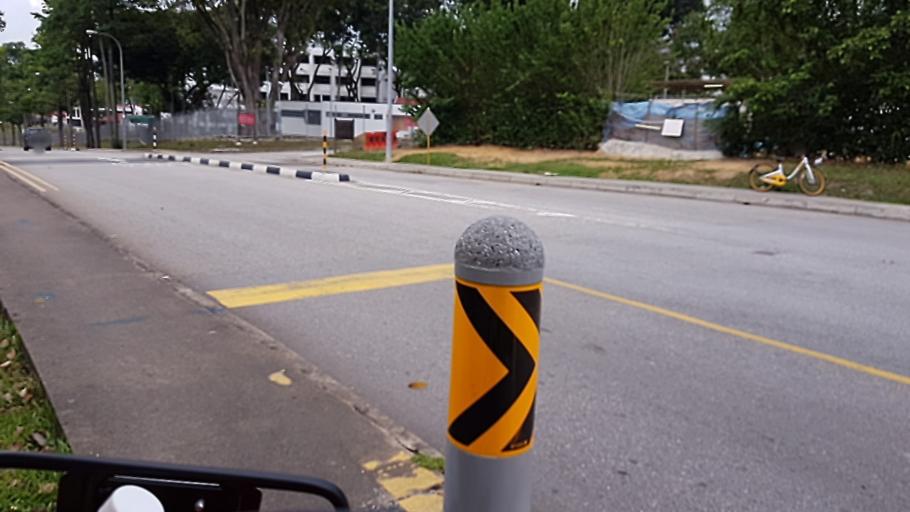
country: MY
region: Johor
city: Kampung Pasir Gudang Baru
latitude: 1.3682
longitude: 103.9776
